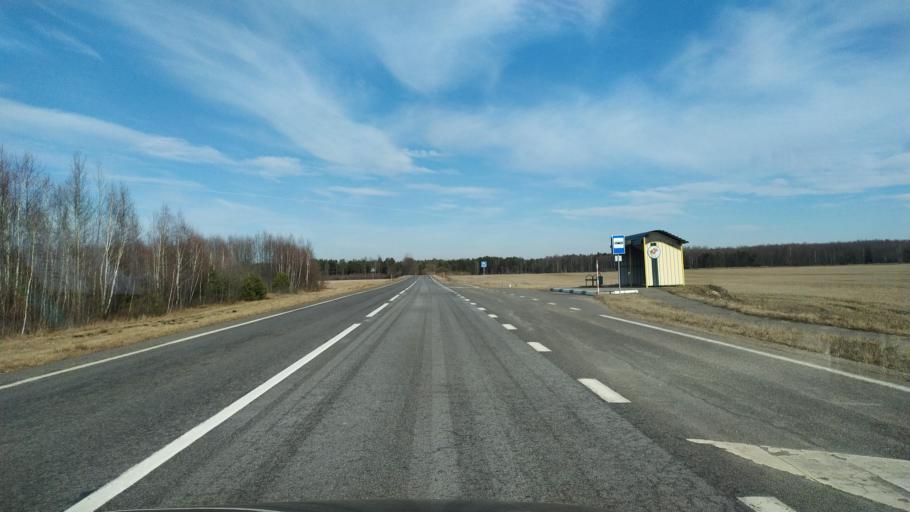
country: BY
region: Brest
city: Zhabinka
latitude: 52.4604
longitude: 24.1418
